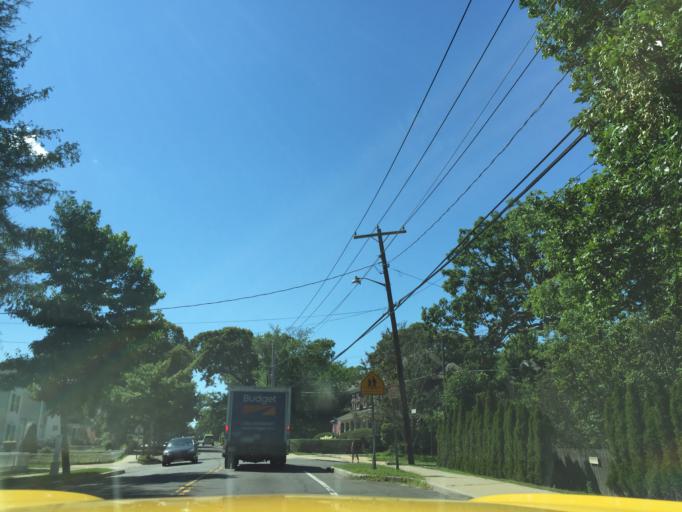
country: US
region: New York
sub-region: Suffolk County
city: Sag Harbor
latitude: 40.9967
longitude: -72.2862
